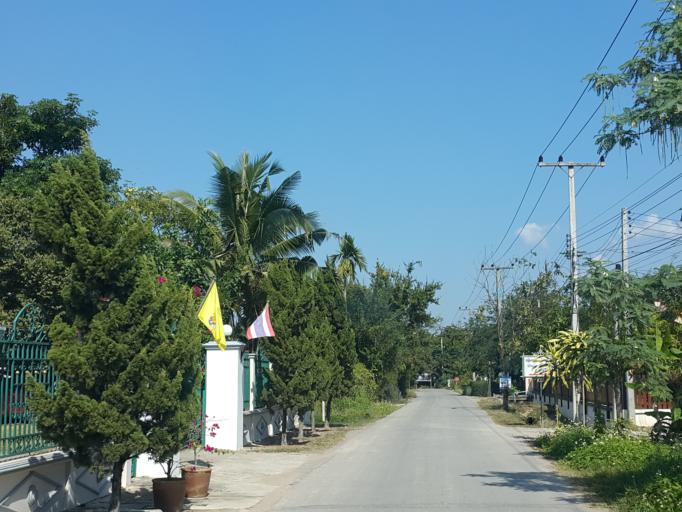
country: TH
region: Chiang Mai
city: San Sai
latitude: 18.9602
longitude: 98.9881
